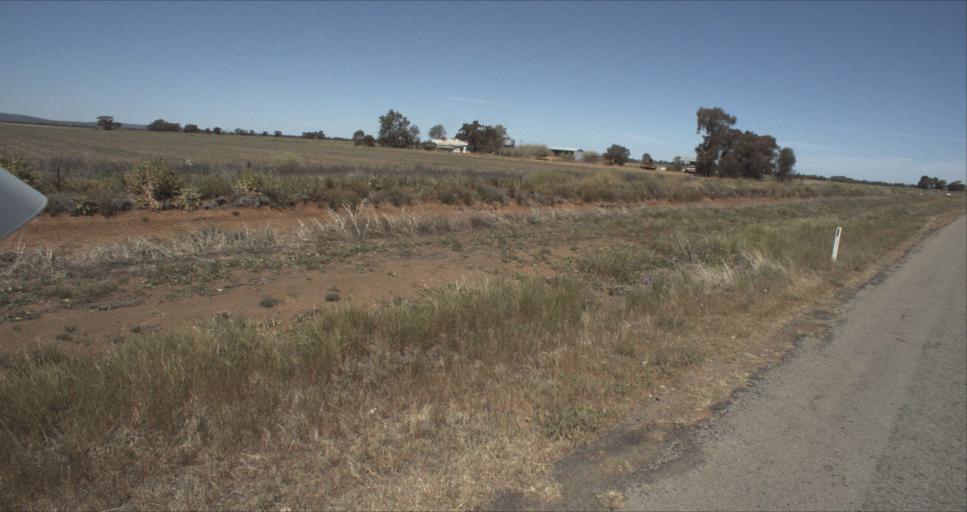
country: AU
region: New South Wales
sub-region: Leeton
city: Leeton
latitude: -34.5030
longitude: 146.3442
